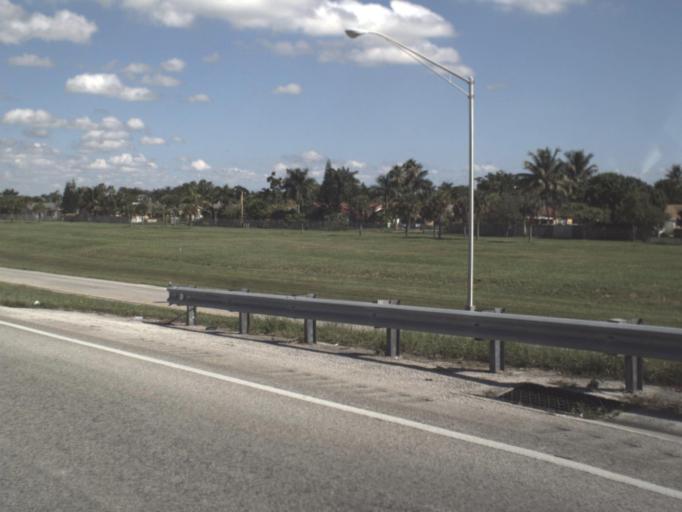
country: US
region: Florida
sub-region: Miami-Dade County
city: Leisure City
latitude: 25.5019
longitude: -80.4171
